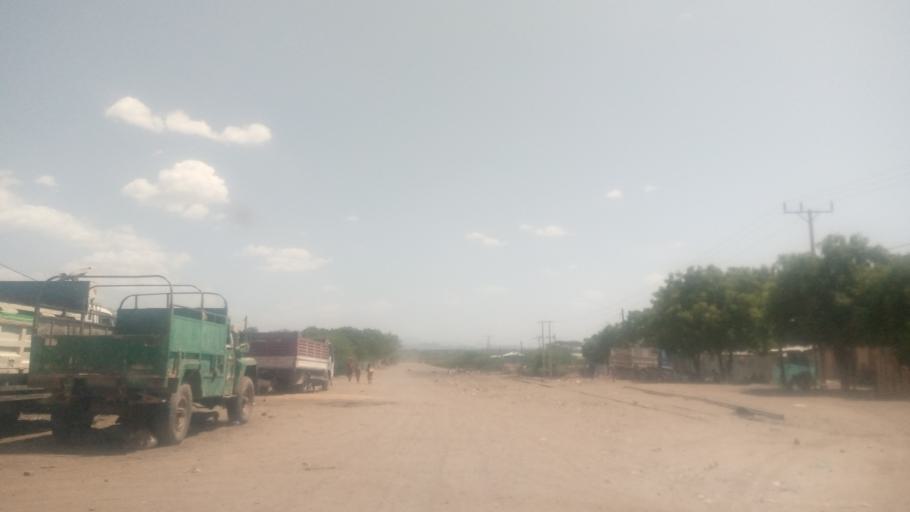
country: ET
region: Oromiya
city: Deder
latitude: 9.5546
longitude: 41.3835
